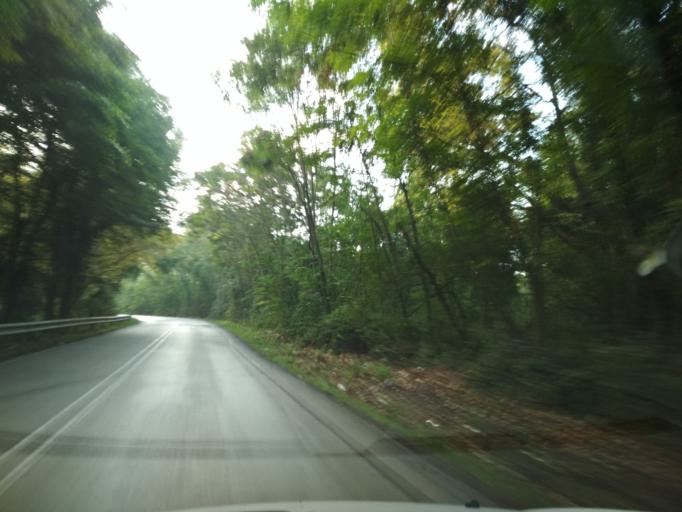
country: GR
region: Central Greece
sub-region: Nomos Evvoias
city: Prokopion
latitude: 38.7501
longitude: 23.4860
